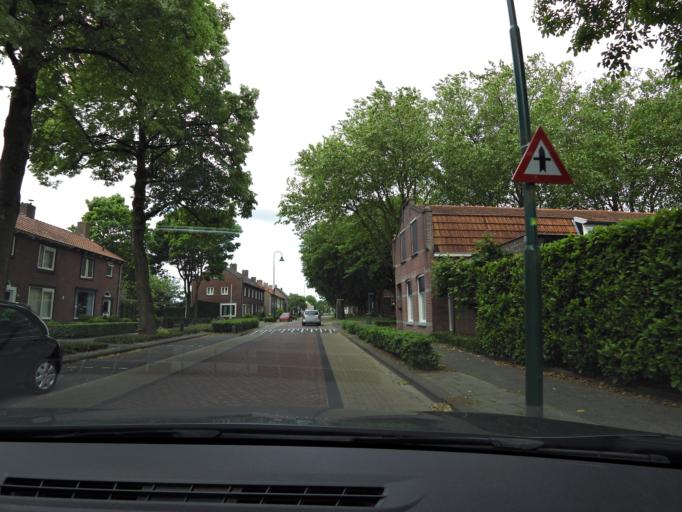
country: NL
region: North Brabant
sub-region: Gemeente Dongen
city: Dongen
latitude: 51.5511
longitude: 4.9433
